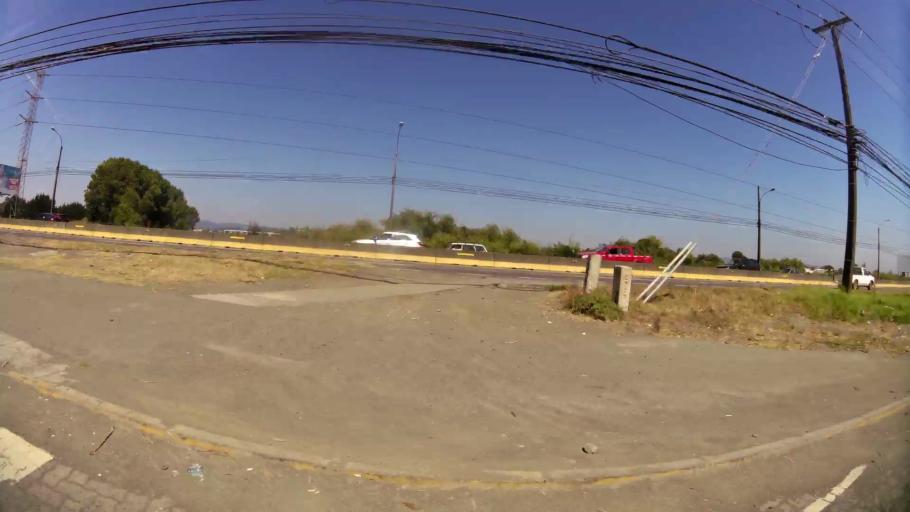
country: CL
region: Biobio
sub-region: Provincia de Concepcion
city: Concepcion
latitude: -36.8019
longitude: -73.0728
